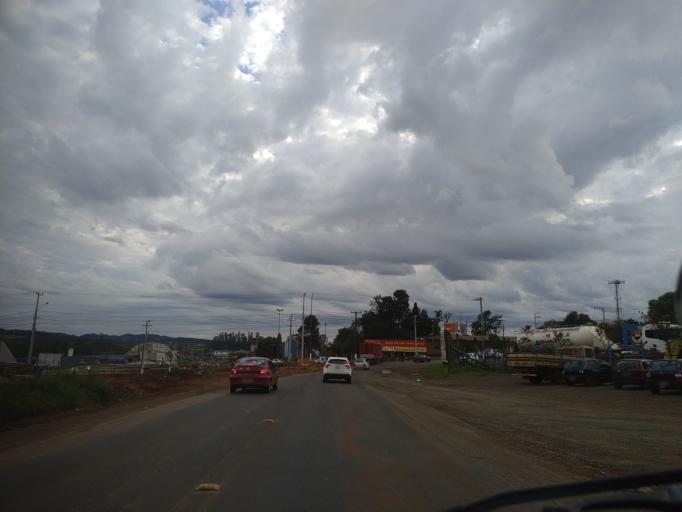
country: BR
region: Santa Catarina
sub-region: Chapeco
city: Chapeco
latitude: -27.0990
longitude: -52.6471
